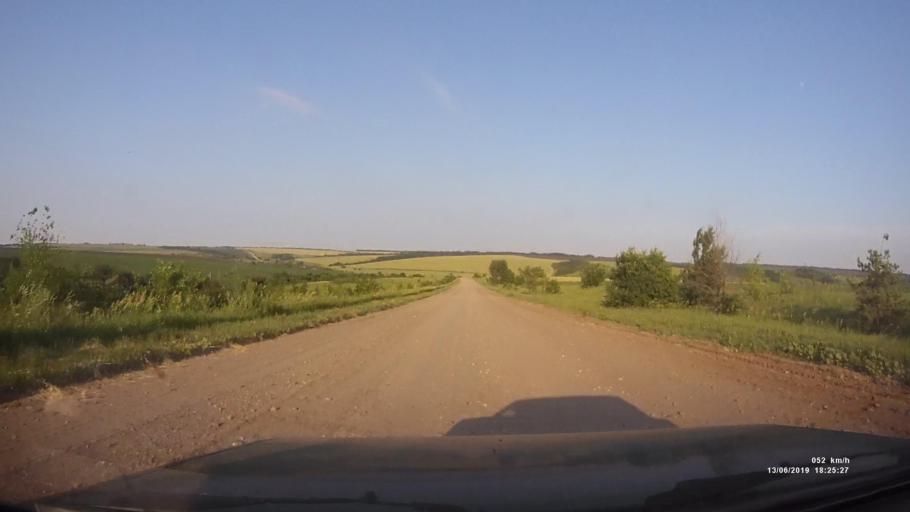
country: RU
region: Rostov
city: Kazanskaya
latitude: 49.8510
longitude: 41.3011
